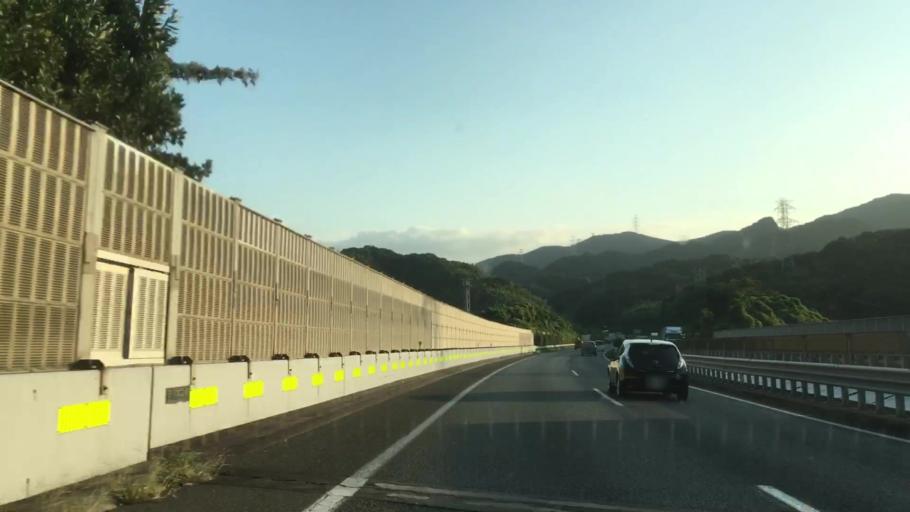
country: JP
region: Yamaguchi
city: Shimonoseki
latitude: 33.9096
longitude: 130.9749
